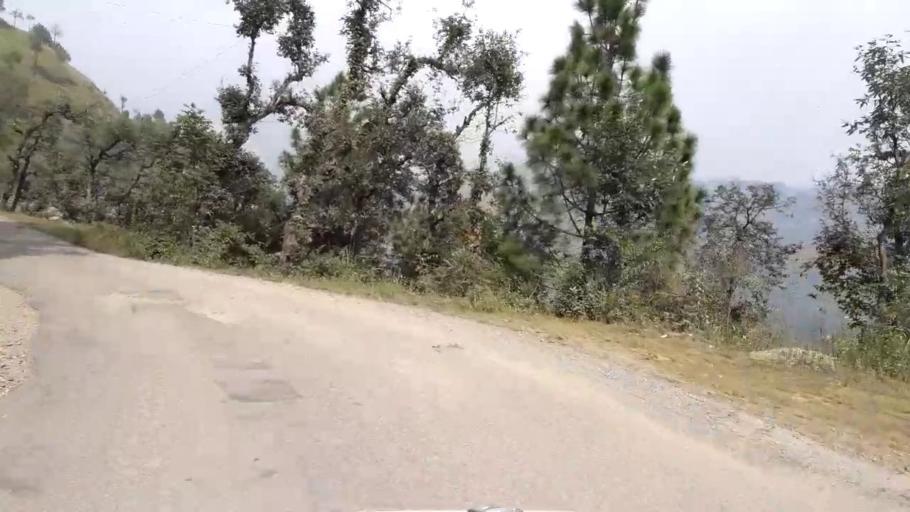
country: IN
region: Himachal Pradesh
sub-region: Shimla
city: Shimla
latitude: 31.0536
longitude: 77.1550
